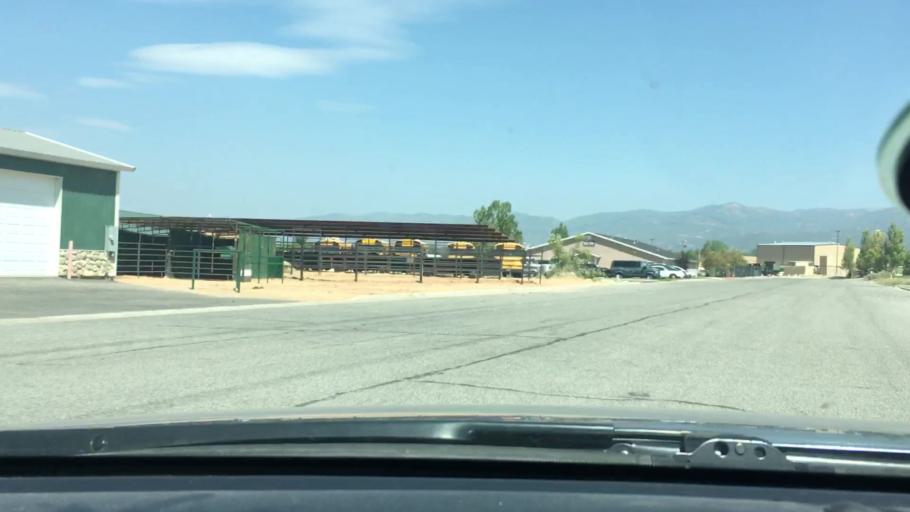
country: US
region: Utah
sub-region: Sanpete County
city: Mount Pleasant
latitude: 39.5291
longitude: -111.4692
